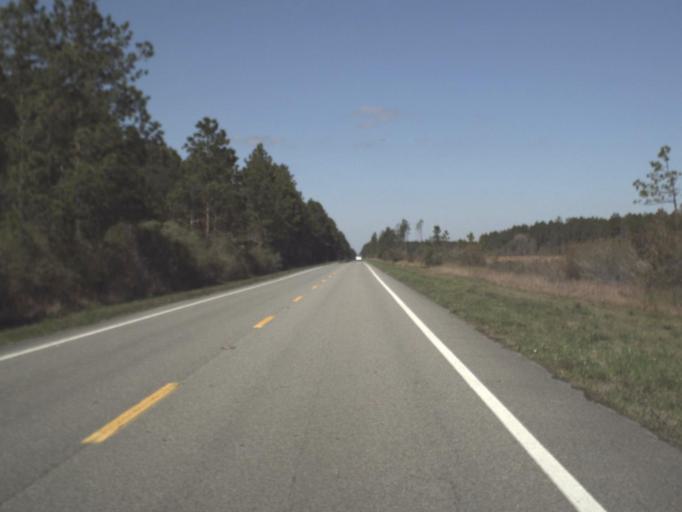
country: US
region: Florida
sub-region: Gulf County
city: Port Saint Joe
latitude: 29.9135
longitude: -85.2032
